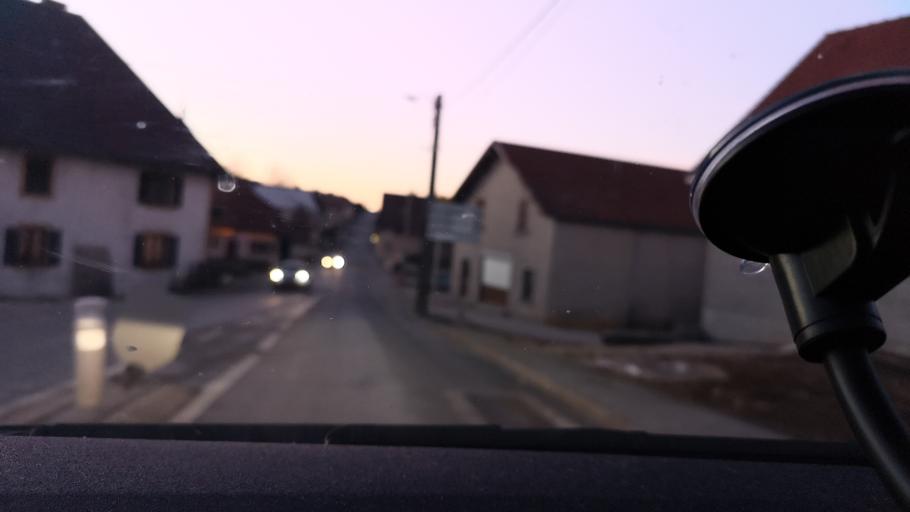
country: FR
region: Franche-Comte
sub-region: Departement du Doubs
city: Frasne
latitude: 46.8135
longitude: 6.0696
